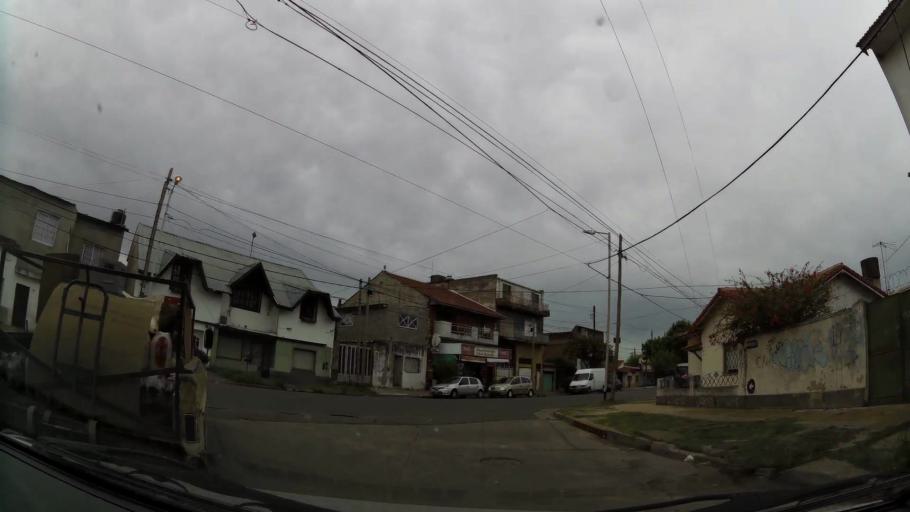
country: AR
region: Buenos Aires
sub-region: Partido de Avellaneda
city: Avellaneda
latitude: -34.6708
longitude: -58.3443
